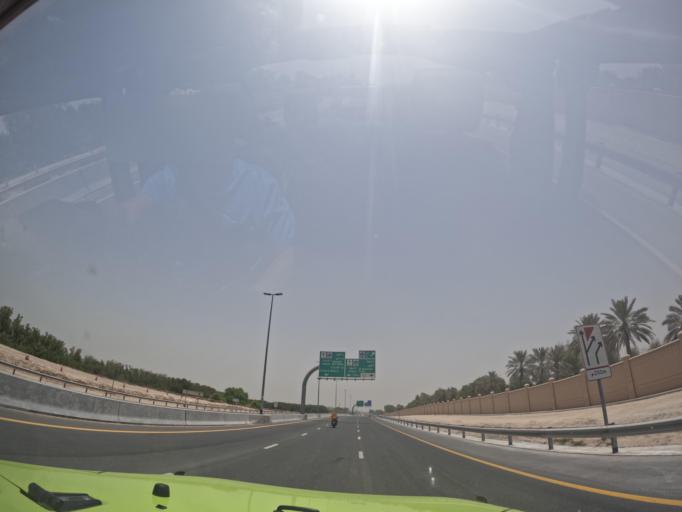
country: AE
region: Dubai
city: Dubai
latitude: 25.1472
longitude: 55.3247
